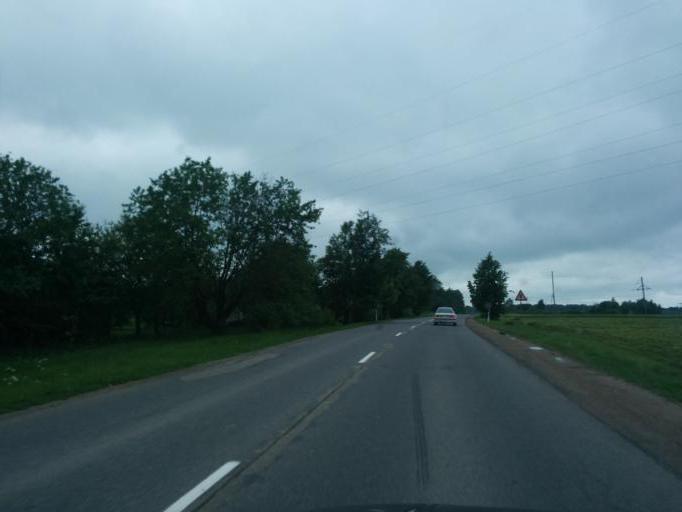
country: LV
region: Smiltene
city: Smiltene
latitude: 57.4315
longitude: 25.8832
